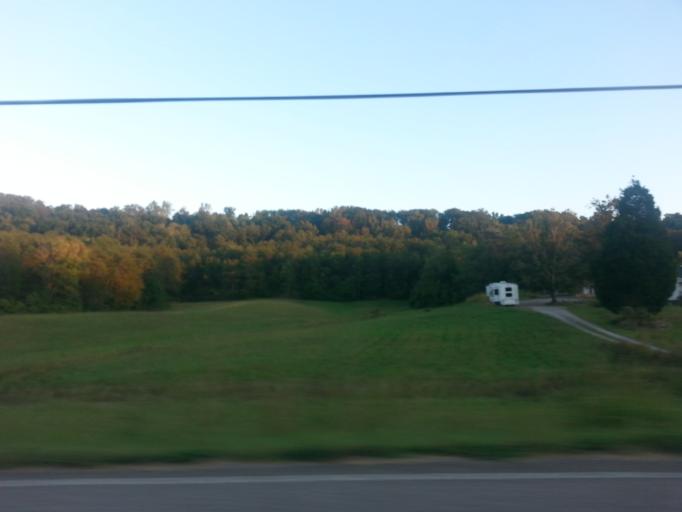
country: US
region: Tennessee
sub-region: Sevier County
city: Seymour
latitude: 35.9199
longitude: -83.7774
